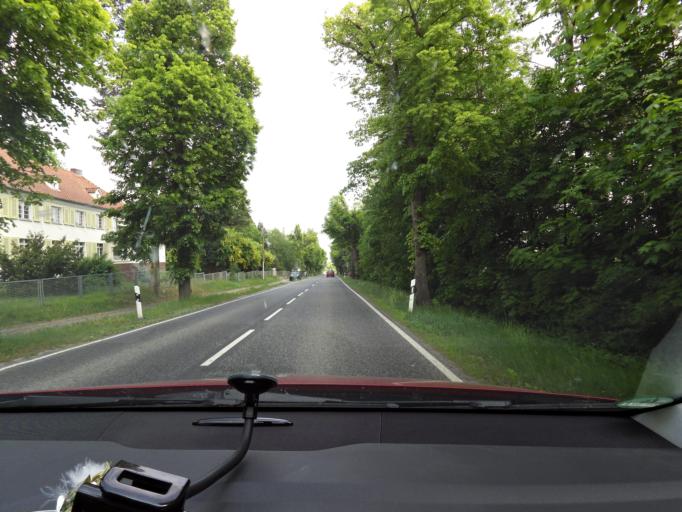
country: DE
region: Thuringia
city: Oberdorla
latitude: 51.2067
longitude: 10.3989
